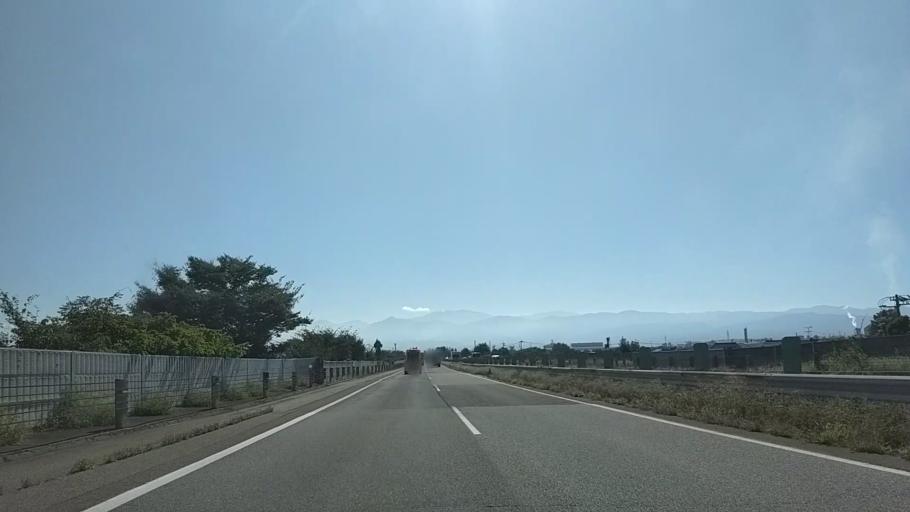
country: JP
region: Toyama
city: Kuragaki-kosugi
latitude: 36.6802
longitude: 137.1548
